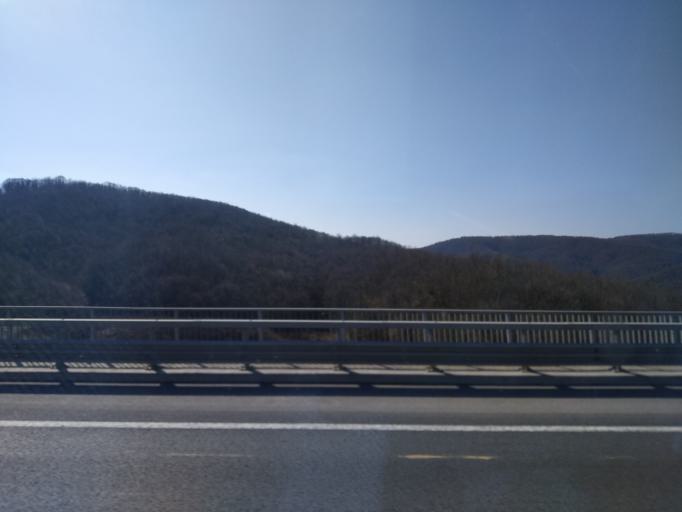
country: TR
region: Istanbul
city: Mahmut Sevket Pasa
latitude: 41.1514
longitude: 29.2697
